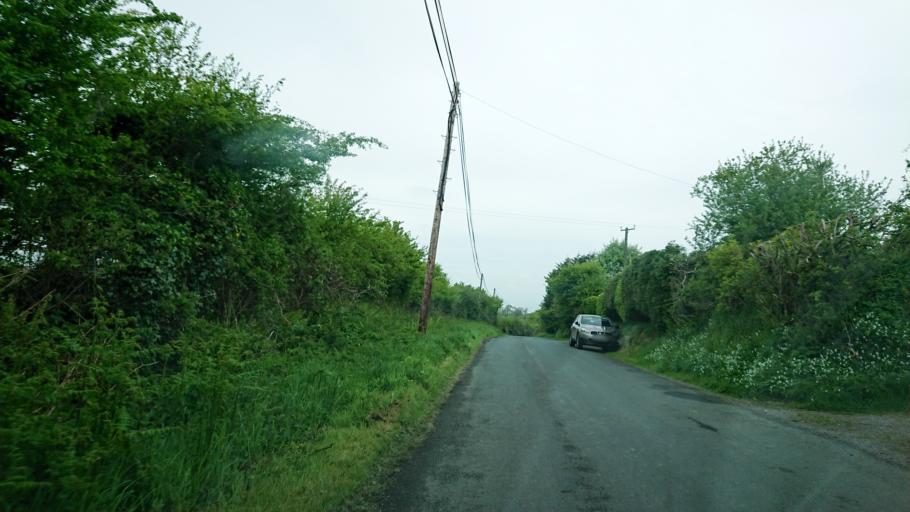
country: IE
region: Munster
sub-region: Waterford
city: Waterford
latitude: 52.2233
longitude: -7.0356
